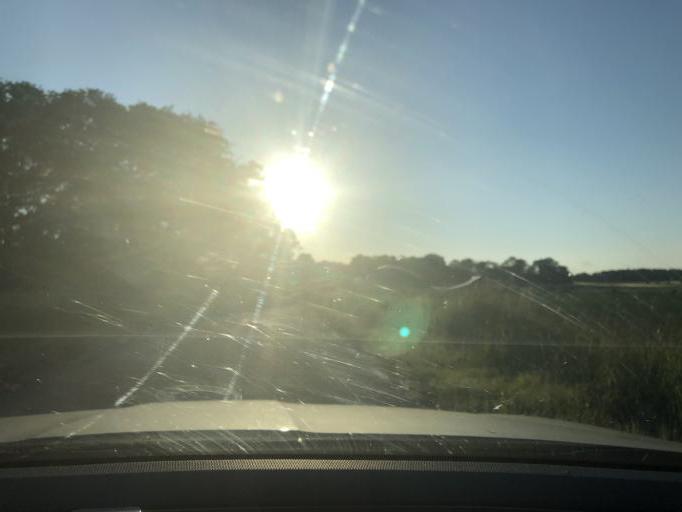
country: SE
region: Blekinge
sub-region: Karlshamns Kommun
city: Morrum
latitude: 56.1407
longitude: 14.6535
